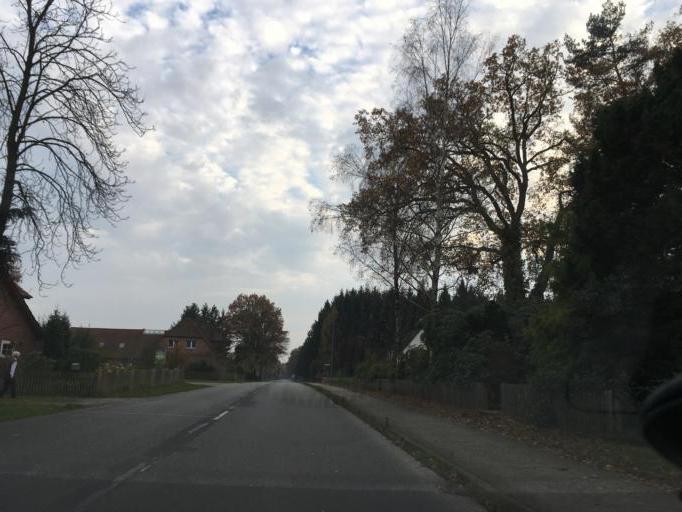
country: DE
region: Lower Saxony
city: Wietzendorf
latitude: 52.9418
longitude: 9.9823
